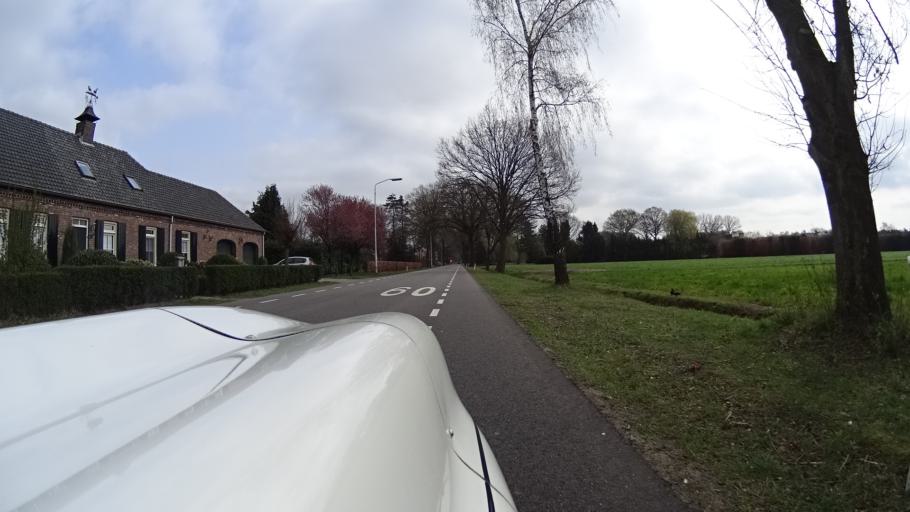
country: NL
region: North Brabant
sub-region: Gemeente Best
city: Best
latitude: 51.5160
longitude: 5.4121
